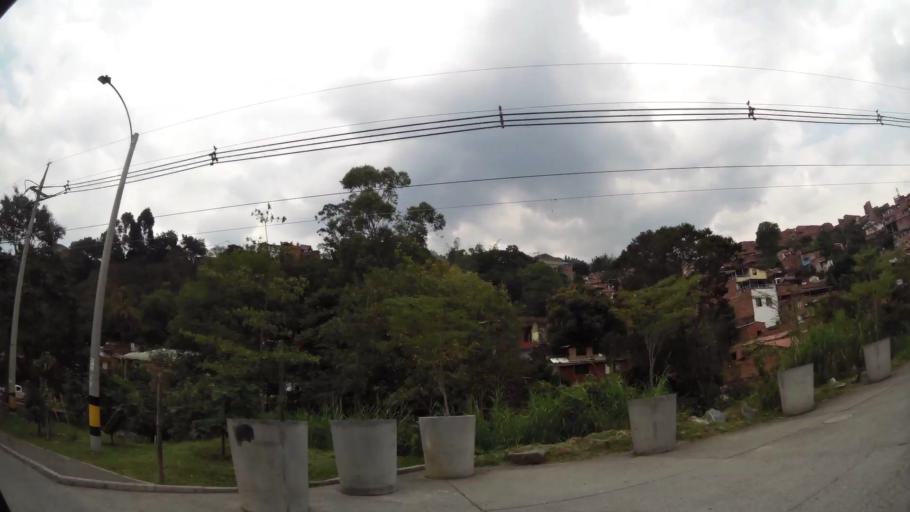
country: CO
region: Antioquia
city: Medellin
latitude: 6.2362
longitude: -75.5422
